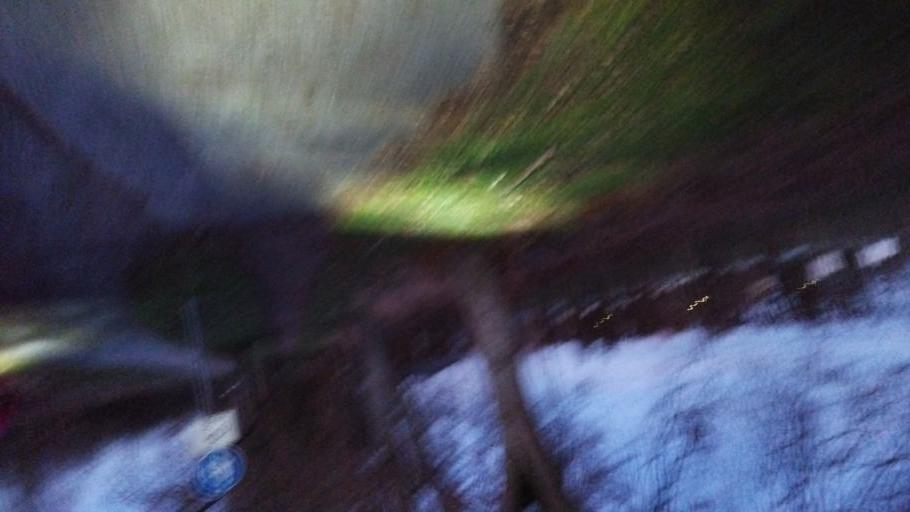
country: DE
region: Bavaria
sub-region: Regierungsbezirk Unterfranken
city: Volkach
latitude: 49.8699
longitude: 10.2160
